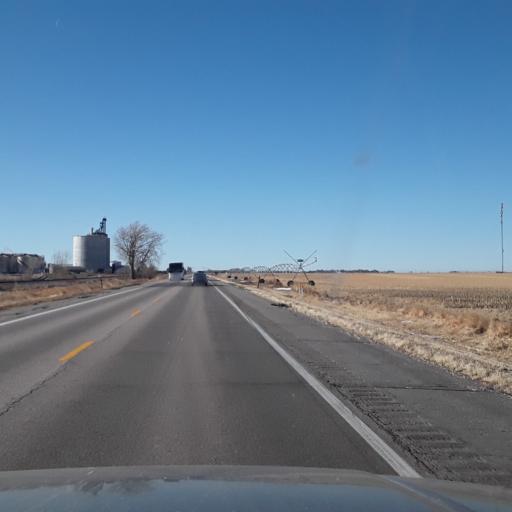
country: US
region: Nebraska
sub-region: Kearney County
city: Minden
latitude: 40.4865
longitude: -99.0674
